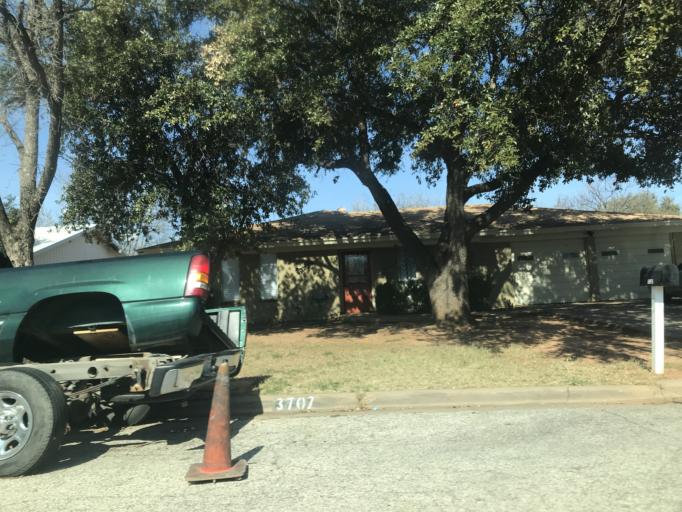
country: US
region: Texas
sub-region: Tom Green County
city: San Angelo
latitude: 31.4314
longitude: -100.4870
